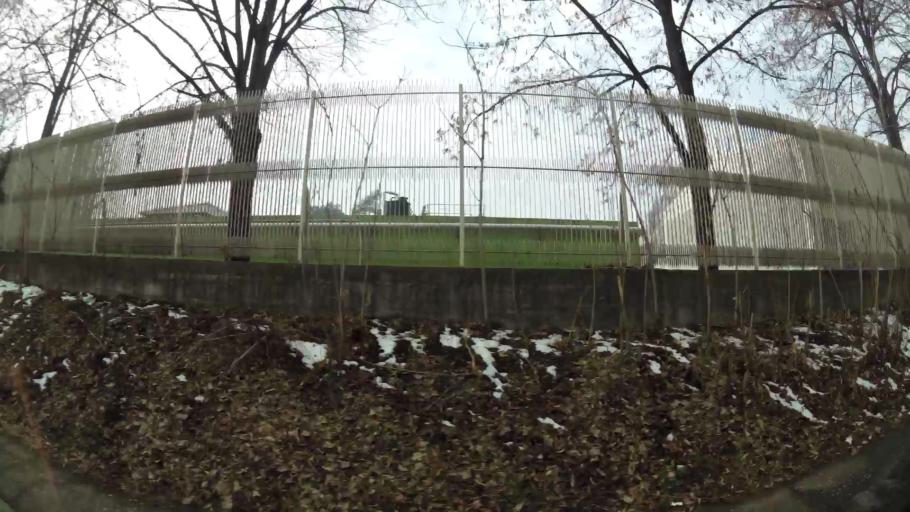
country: MK
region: Cair
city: Cair
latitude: 41.9979
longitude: 21.4691
